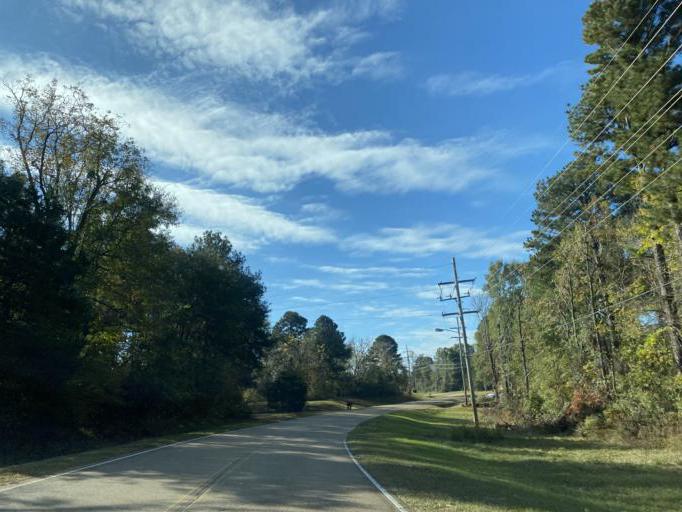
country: US
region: Mississippi
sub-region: Madison County
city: Madison
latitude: 32.4813
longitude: -90.1772
